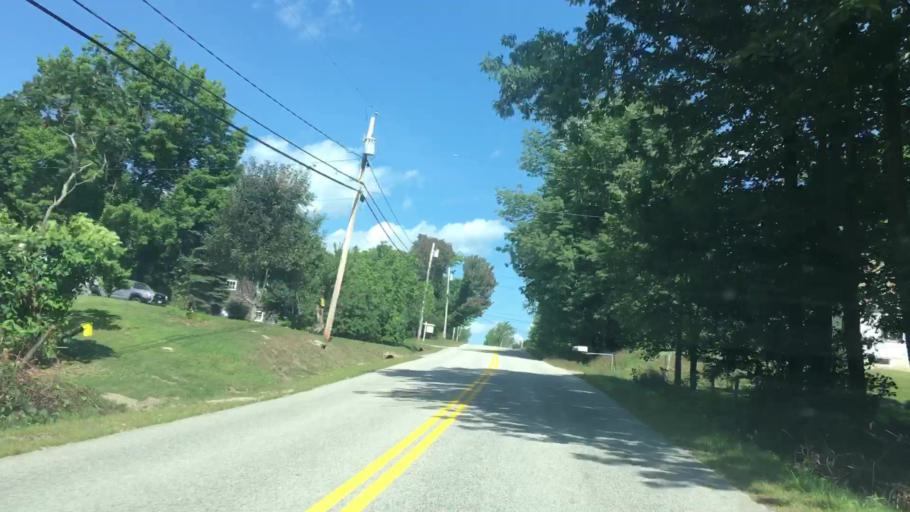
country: US
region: Maine
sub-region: Cumberland County
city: New Gloucester
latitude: 43.9413
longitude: -70.3008
